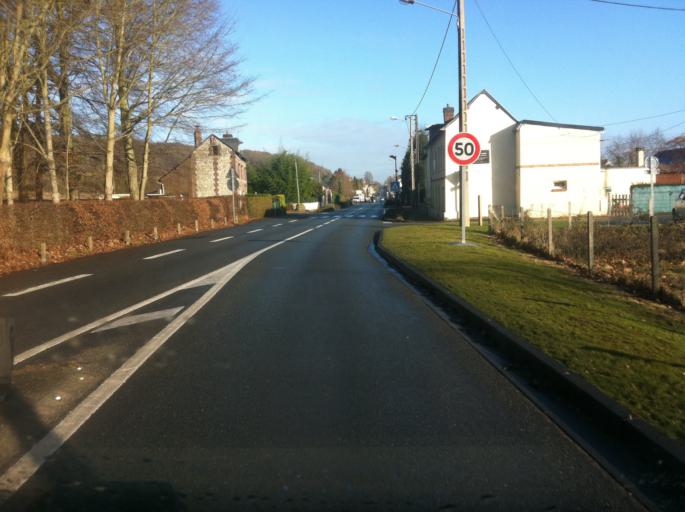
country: FR
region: Haute-Normandie
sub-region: Departement de la Seine-Maritime
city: Duclair
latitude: 49.4685
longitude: 0.8570
